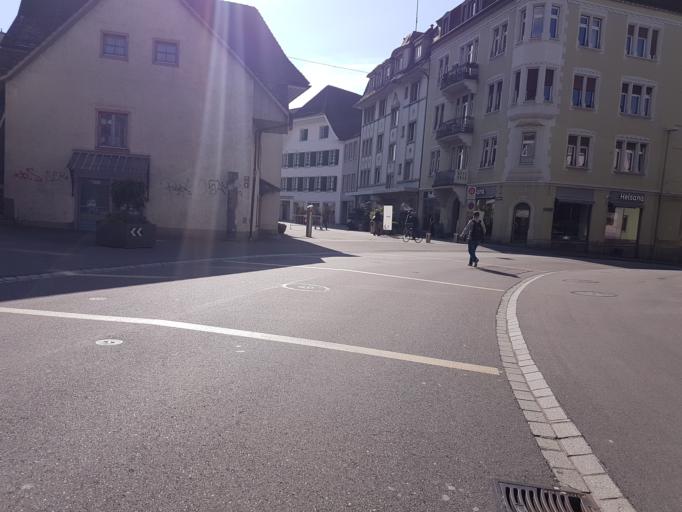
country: CH
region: Solothurn
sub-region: Bezirk Olten
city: Olten
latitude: 47.3499
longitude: 7.9003
